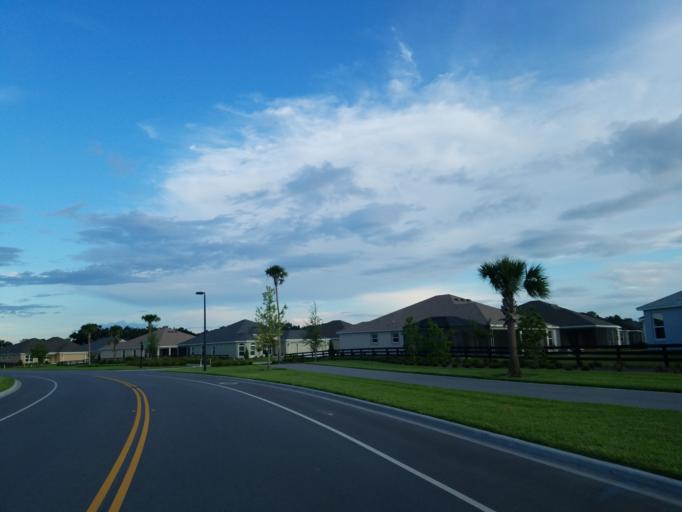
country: US
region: Florida
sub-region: Sumter County
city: Wildwood
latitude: 28.7930
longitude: -82.0247
